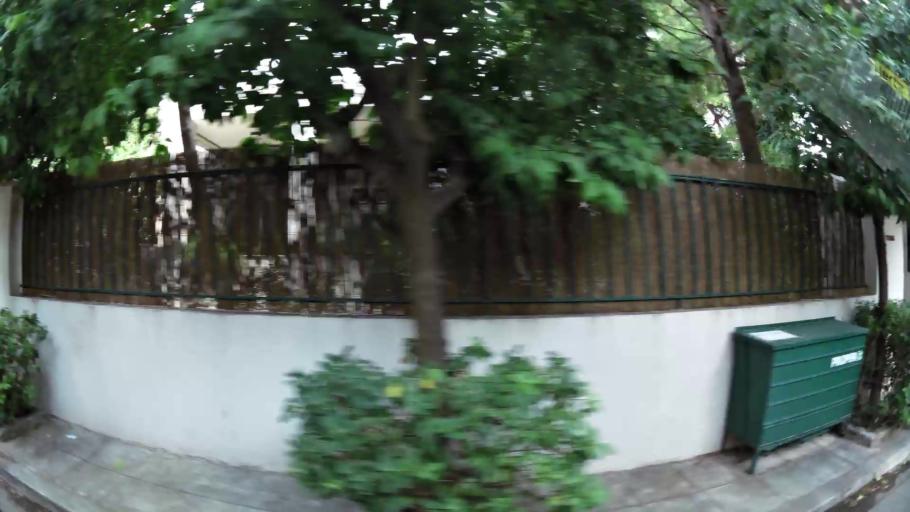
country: GR
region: Attica
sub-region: Nomarchia Athinas
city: Neo Psychiko
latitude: 38.0129
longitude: 23.7809
